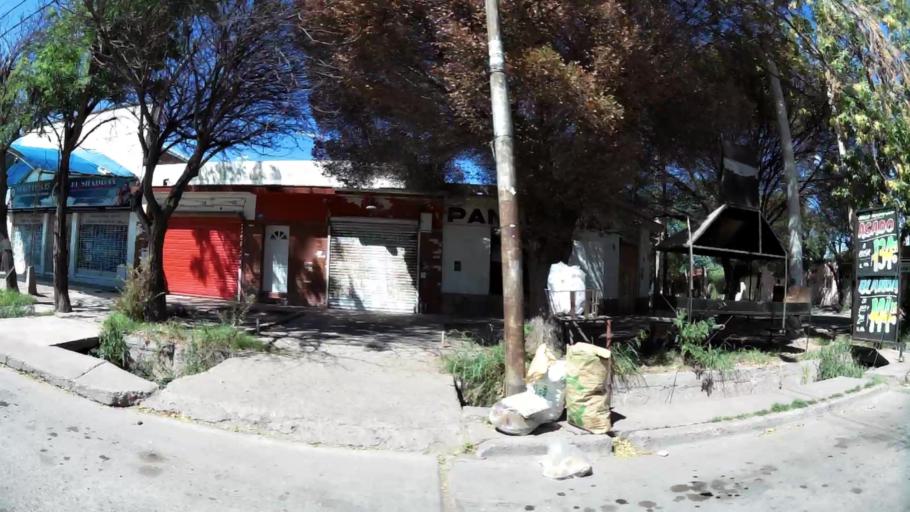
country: AR
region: Mendoza
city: Las Heras
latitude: -32.8459
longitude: -68.8340
